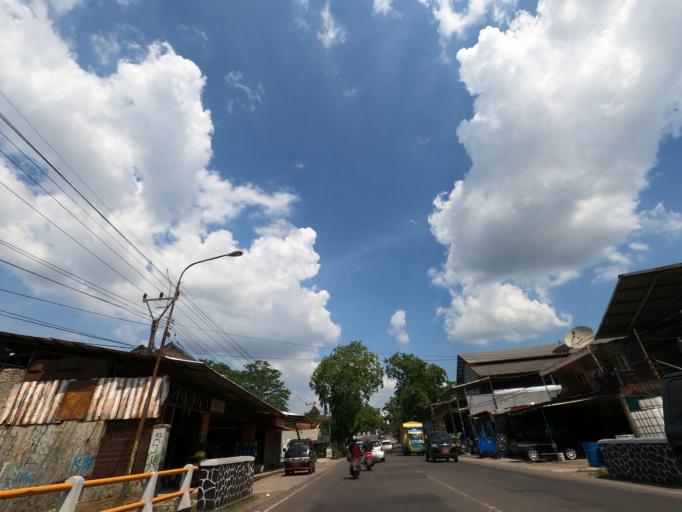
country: ID
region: West Java
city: Pamanukan
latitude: -6.5540
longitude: 107.7569
